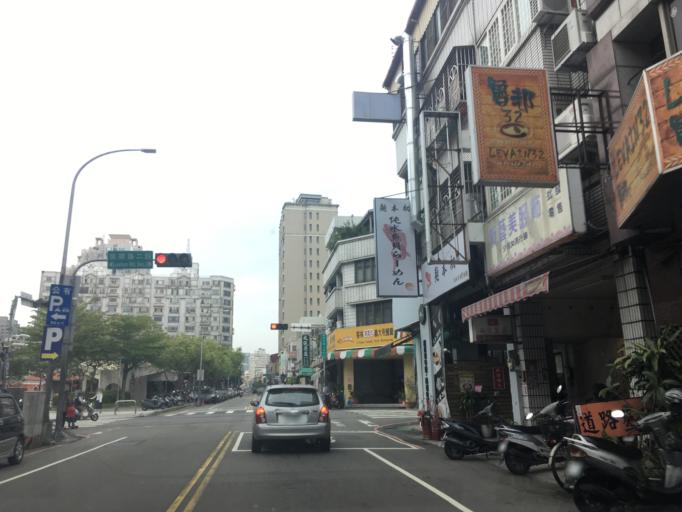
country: TW
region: Taiwan
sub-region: Taichung City
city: Taichung
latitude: 24.1740
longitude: 120.6879
